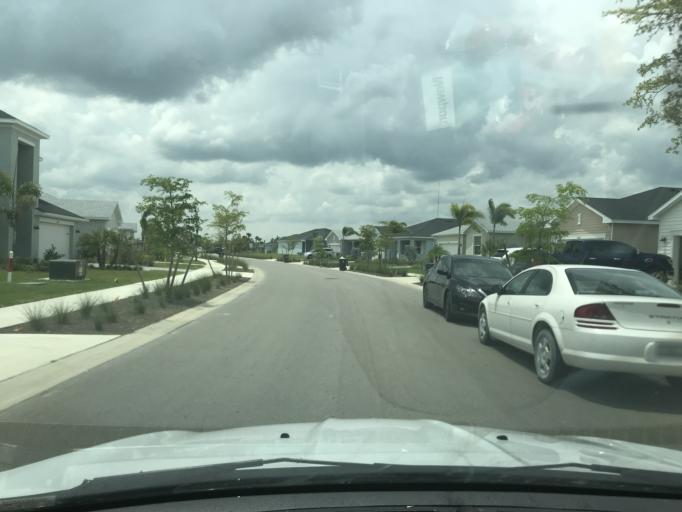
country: US
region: Florida
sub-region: Lee County
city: Olga
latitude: 26.7778
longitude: -81.7395
